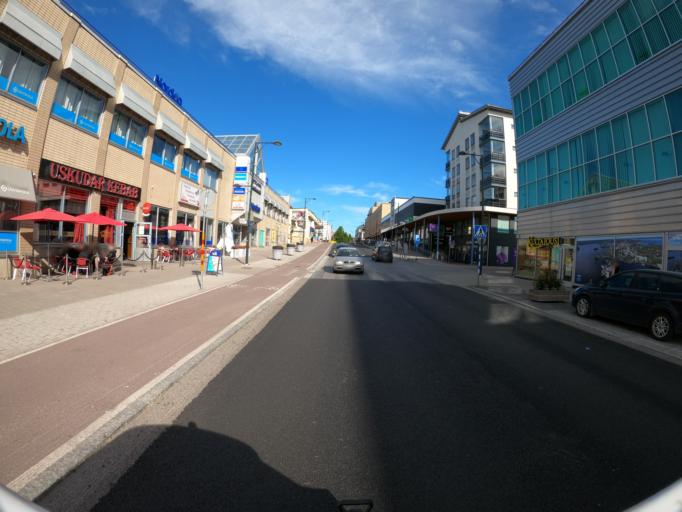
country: FI
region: Southern Savonia
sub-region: Savonlinna
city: Savonlinna
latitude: 61.8704
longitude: 28.8772
